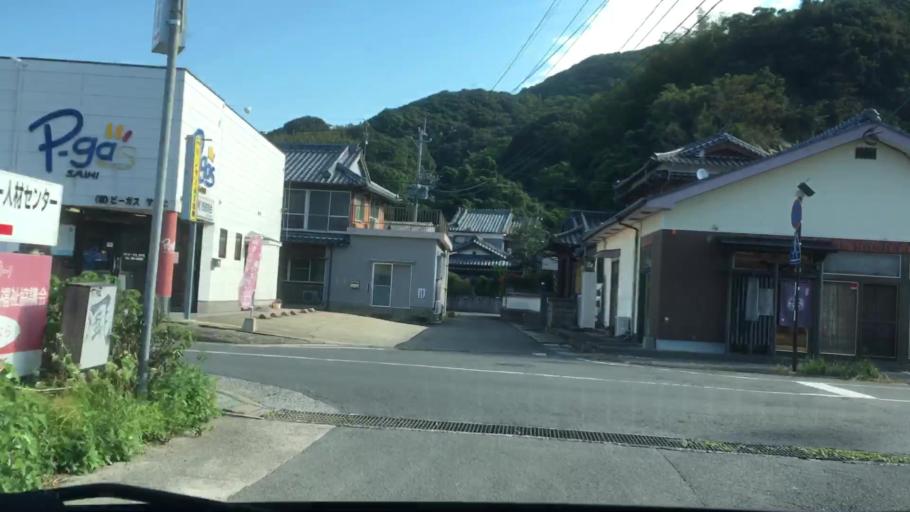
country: JP
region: Nagasaki
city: Sasebo
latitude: 32.9448
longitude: 129.6385
